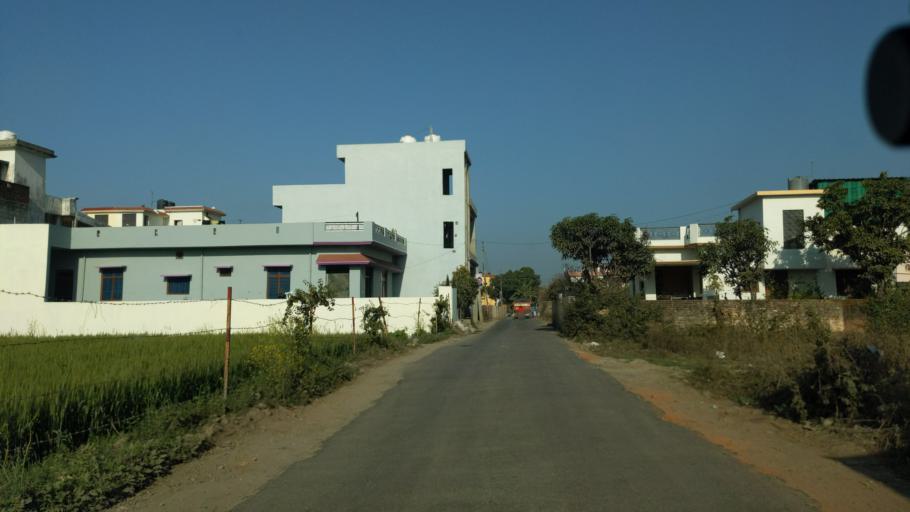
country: IN
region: Uttarakhand
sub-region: Naini Tal
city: Haldwani
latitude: 29.2098
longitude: 79.4918
